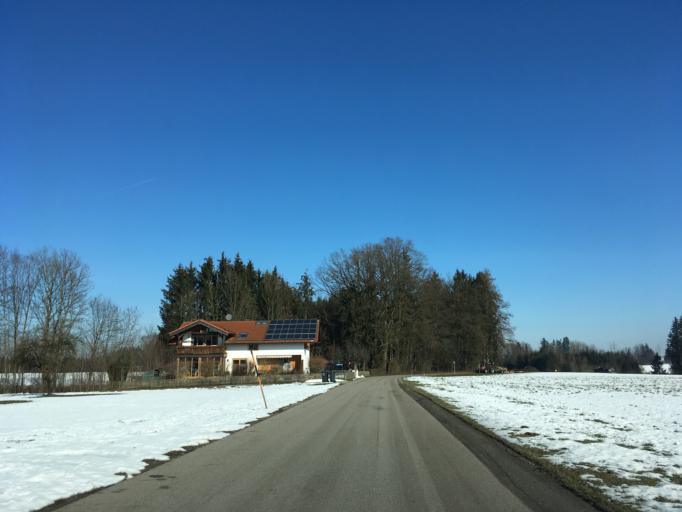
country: DE
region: Bavaria
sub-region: Upper Bavaria
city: Vogtareuth
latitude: 47.9306
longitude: 12.1663
